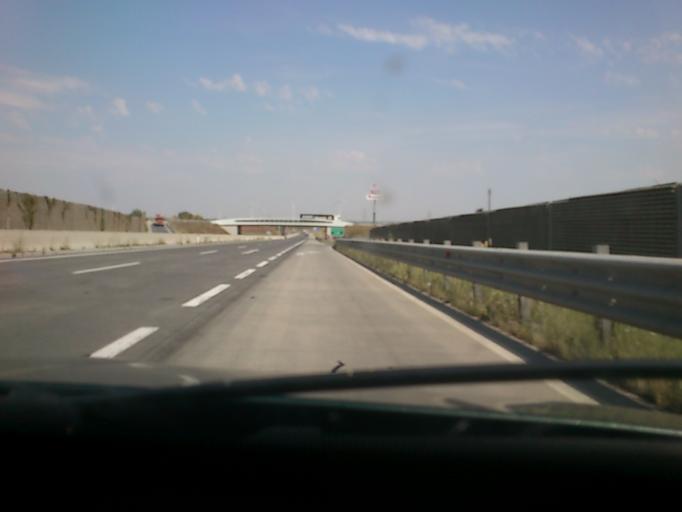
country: AT
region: Lower Austria
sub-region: Politischer Bezirk Ganserndorf
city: Aderklaa
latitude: 48.3075
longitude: 16.5120
